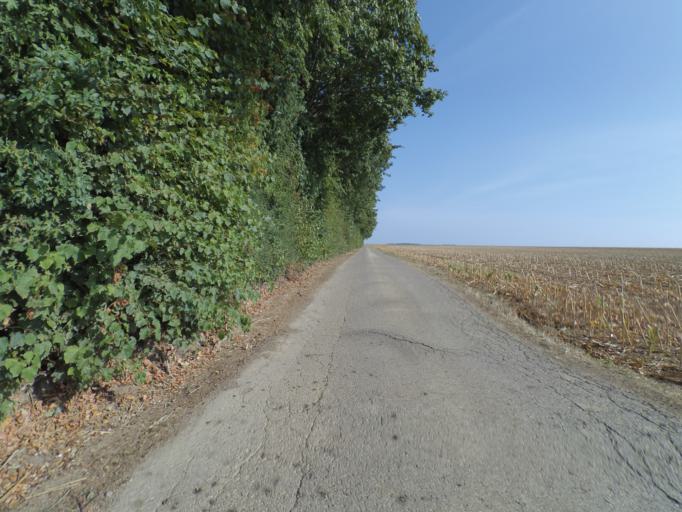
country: DE
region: Rheinland-Pfalz
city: Merzkirchen
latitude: 49.5670
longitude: 6.4788
